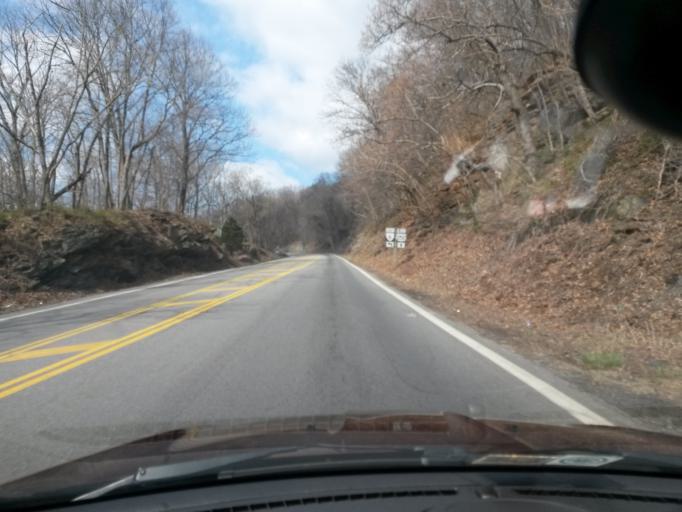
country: US
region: Virginia
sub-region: City of Waynesboro
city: Waynesboro
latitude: 38.0382
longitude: -78.8341
